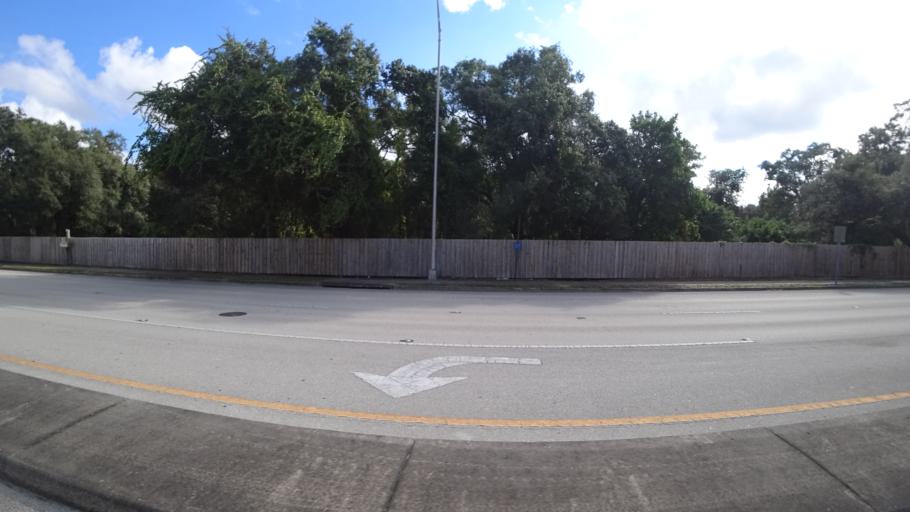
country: US
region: Florida
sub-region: Sarasota County
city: North Sarasota
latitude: 27.4076
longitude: -82.5054
